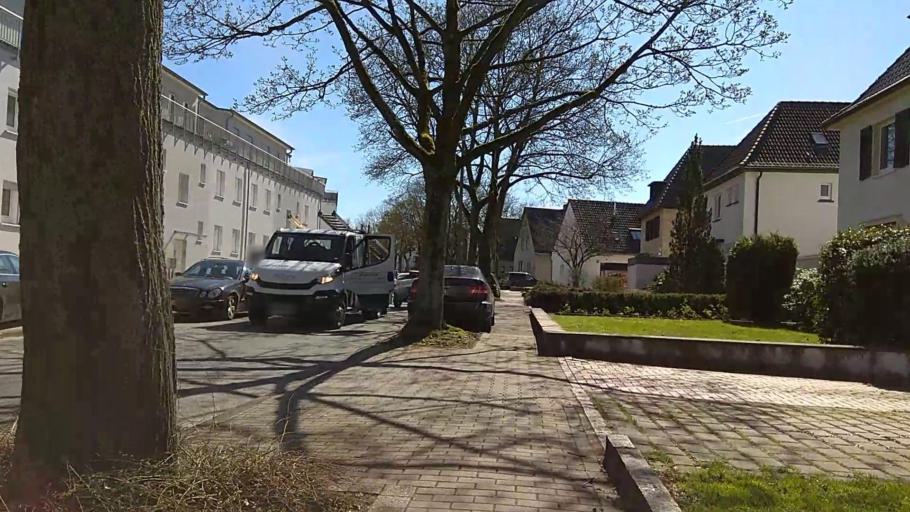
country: DE
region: North Rhine-Westphalia
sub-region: Regierungsbezirk Munster
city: Gladbeck
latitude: 51.5788
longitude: 7.0415
